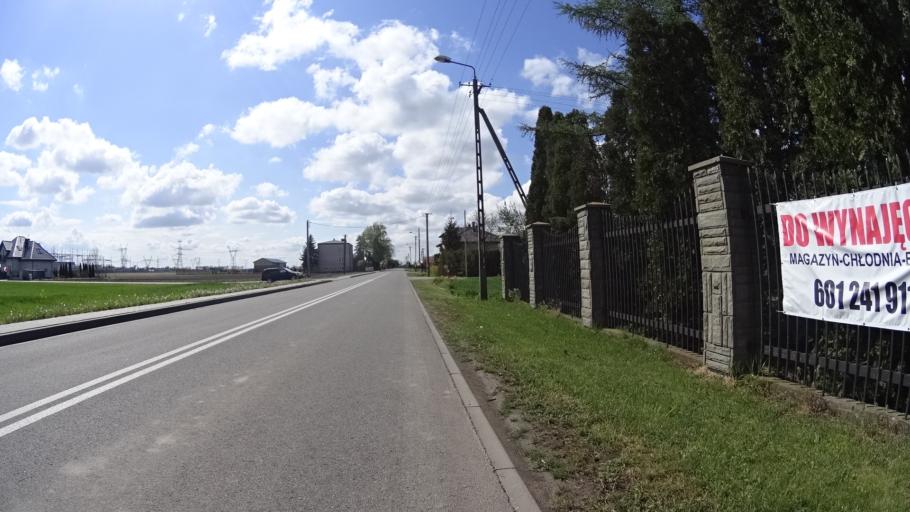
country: PL
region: Masovian Voivodeship
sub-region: Powiat warszawski zachodni
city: Ozarow Mazowiecki
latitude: 52.2309
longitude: 20.7480
